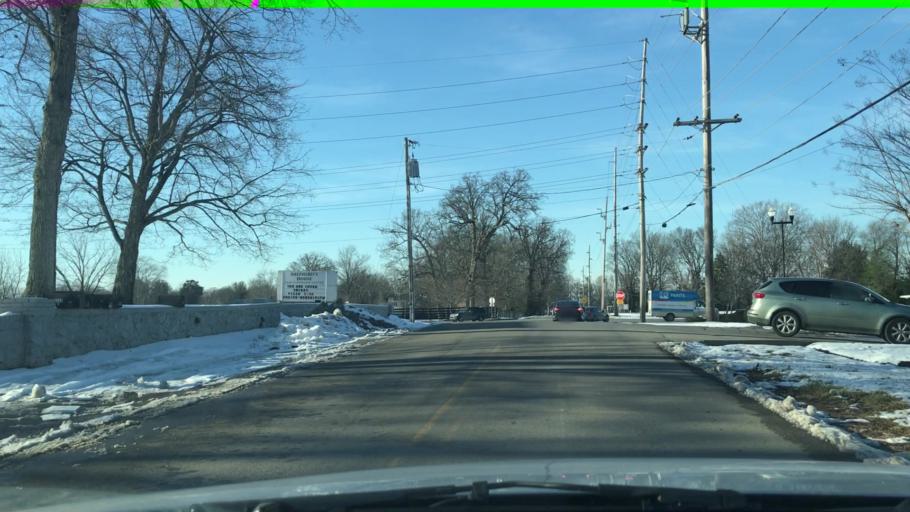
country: US
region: Kentucky
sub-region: Warren County
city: Bowling Green
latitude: 36.9801
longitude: -86.3961
